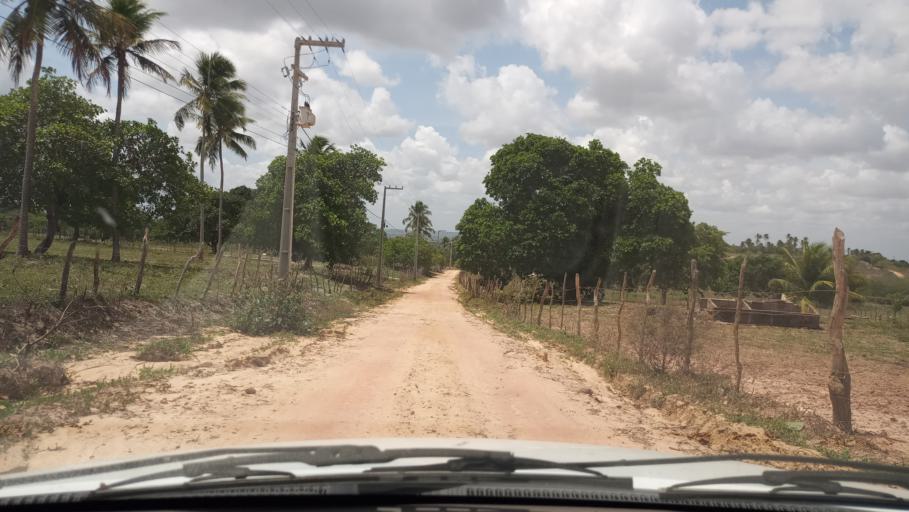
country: BR
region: Rio Grande do Norte
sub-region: Brejinho
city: Brejinho
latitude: -6.2530
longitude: -35.3367
